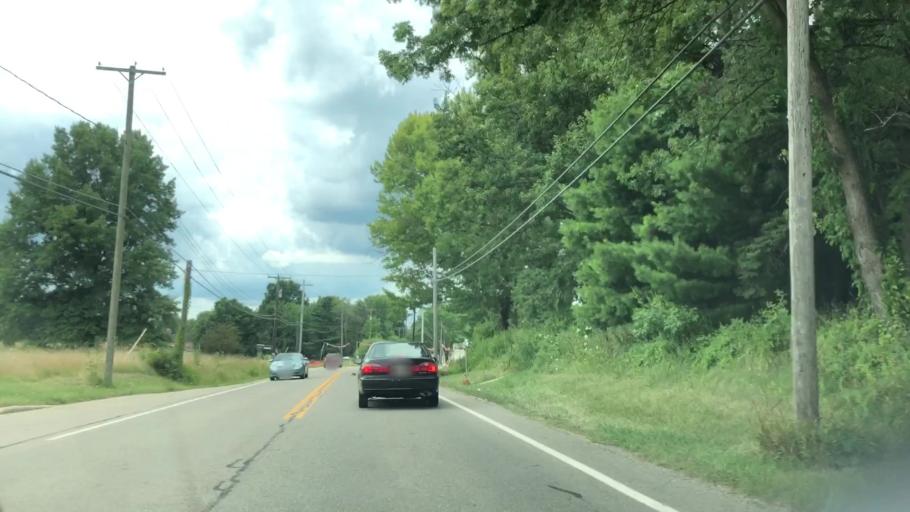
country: US
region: Ohio
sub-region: Summit County
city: Greensburg
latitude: 40.9308
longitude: -81.4562
